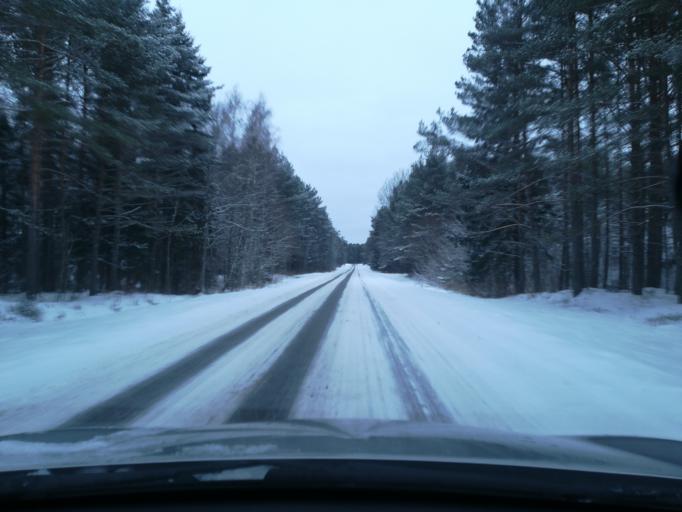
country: EE
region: Harju
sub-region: Keila linn
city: Keila
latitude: 59.3882
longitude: 24.2964
